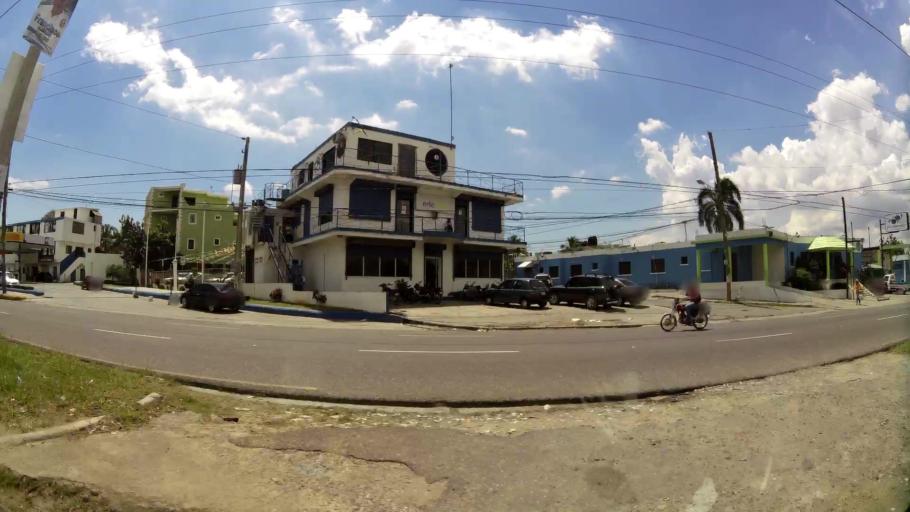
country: DO
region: Santo Domingo
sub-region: Santo Domingo
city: Santo Domingo Este
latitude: 18.5443
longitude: -69.8644
